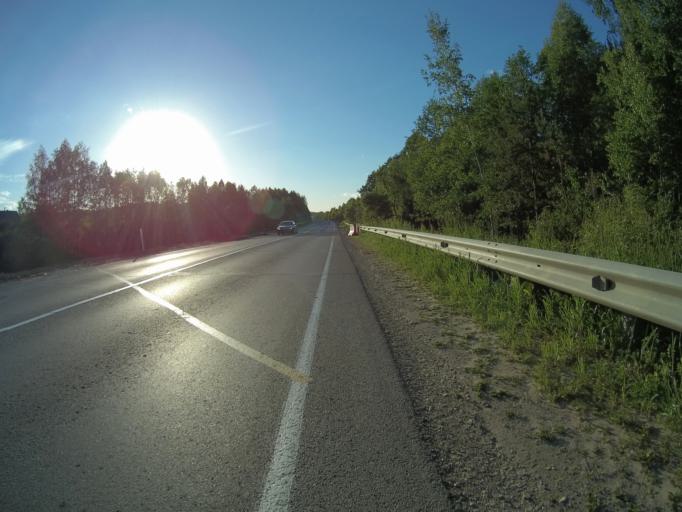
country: RU
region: Vladimir
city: Golovino
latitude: 55.9464
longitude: 40.5818
